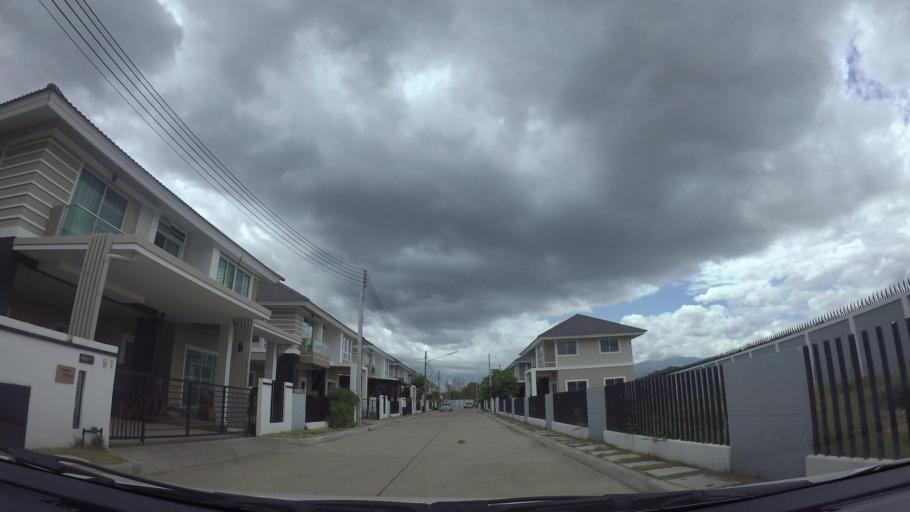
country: TH
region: Chiang Mai
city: Saraphi
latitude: 18.7507
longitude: 99.0439
